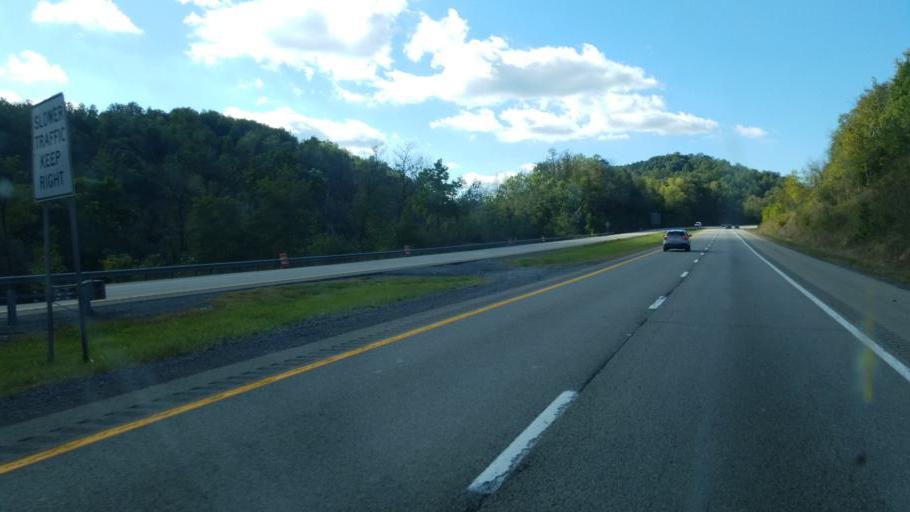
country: US
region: West Virginia
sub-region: Monongalia County
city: Star City
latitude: 39.6675
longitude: -80.0229
